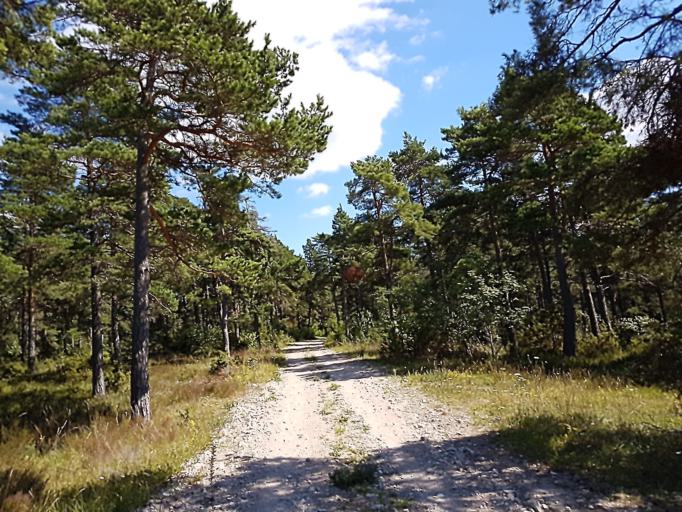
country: SE
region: Gotland
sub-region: Gotland
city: Visby
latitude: 57.6087
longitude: 18.3335
